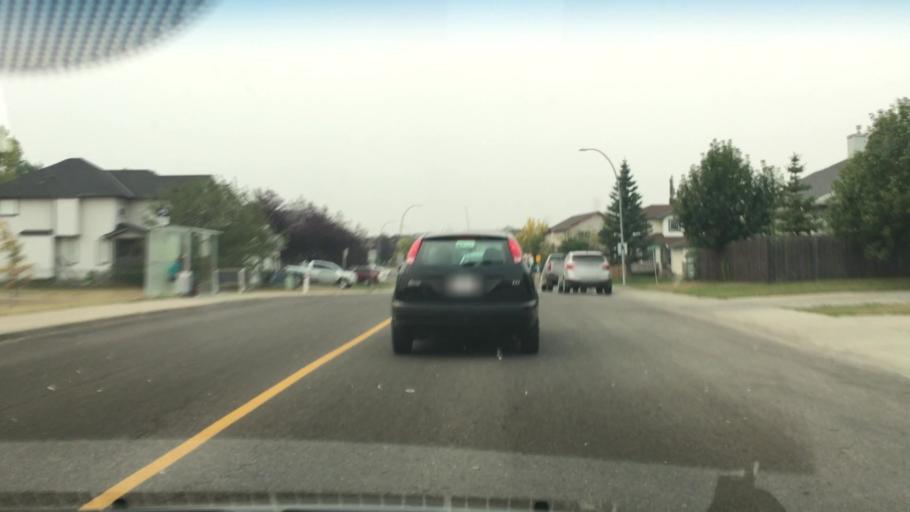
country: CA
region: Alberta
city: Calgary
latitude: 51.1507
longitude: -114.1202
